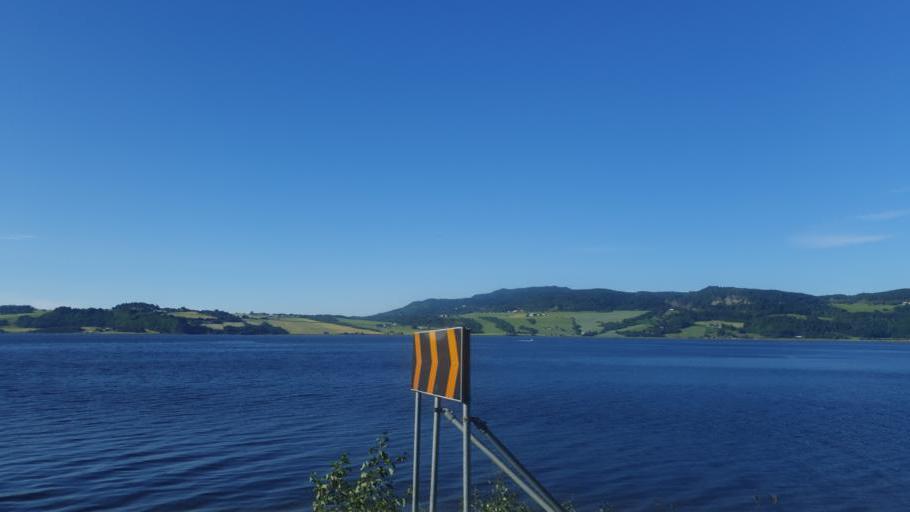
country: NO
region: Sor-Trondelag
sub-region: Melhus
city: Melhus
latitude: 63.3214
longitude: 10.1955
